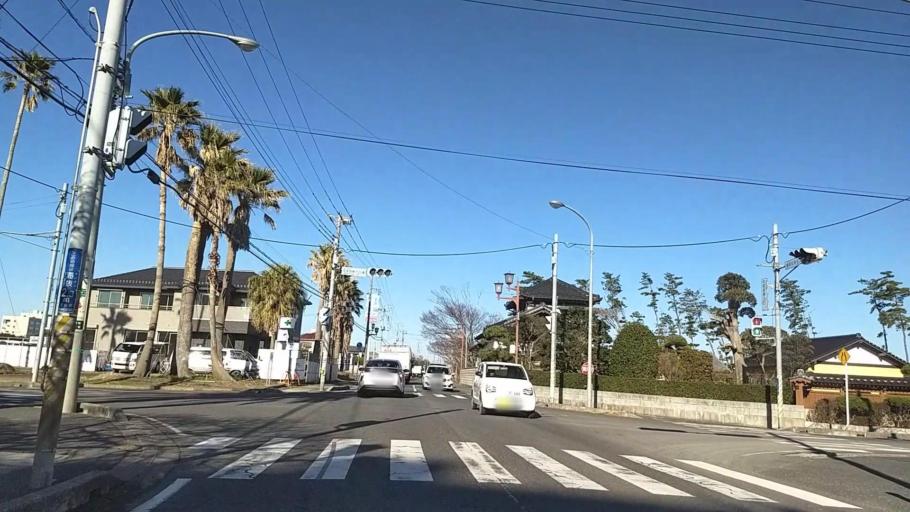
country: JP
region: Chiba
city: Mobara
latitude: 35.4313
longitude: 140.3963
